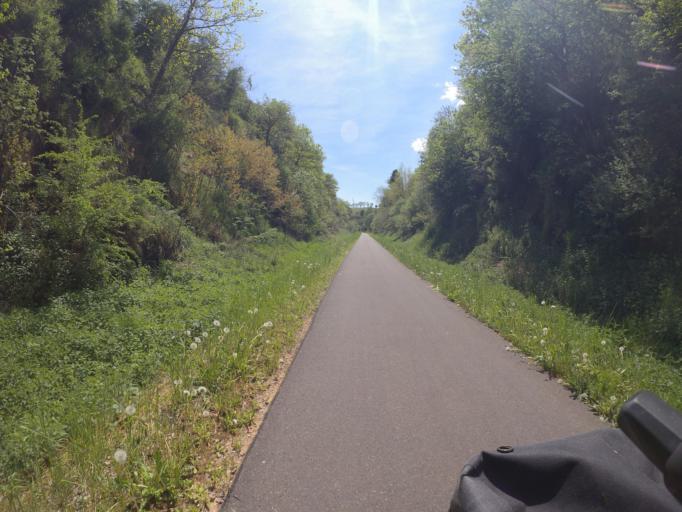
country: DE
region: Rheinland-Pfalz
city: Hallschlag
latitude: 50.3522
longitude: 6.4345
